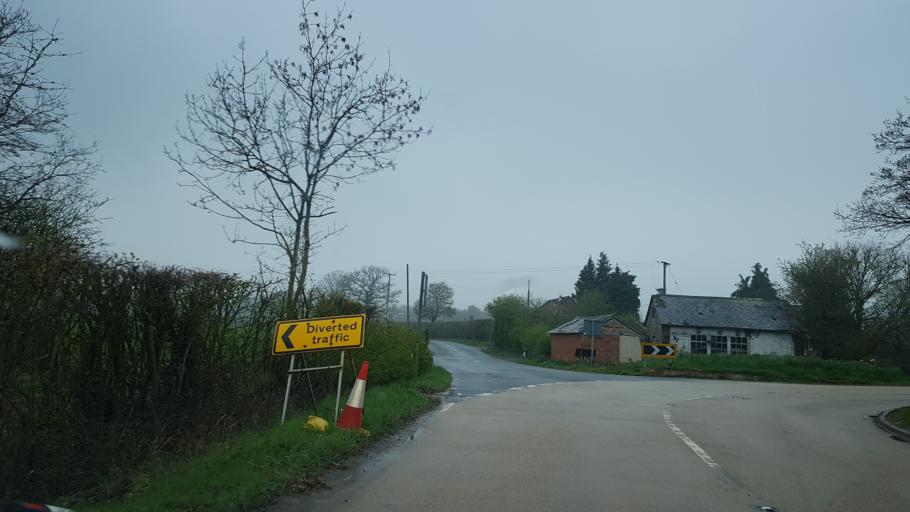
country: GB
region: England
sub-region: Herefordshire
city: Evesbatch
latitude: 52.0827
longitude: -2.4559
